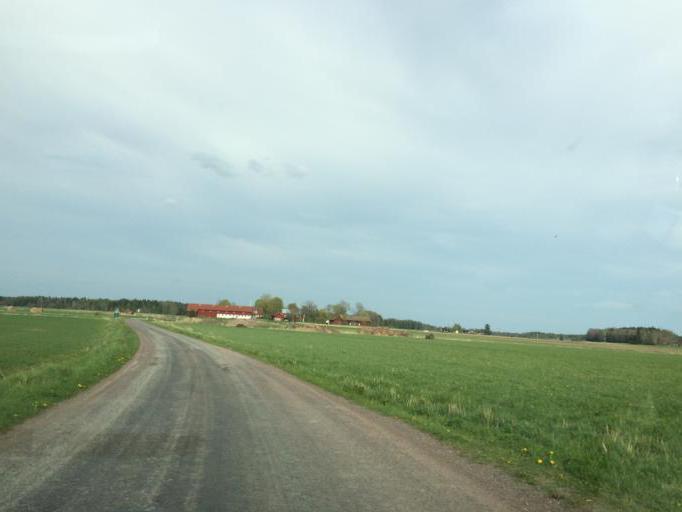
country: SE
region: Vaestmanland
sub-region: Hallstahammars Kommun
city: Hallstahammar
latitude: 59.6012
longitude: 16.1121
